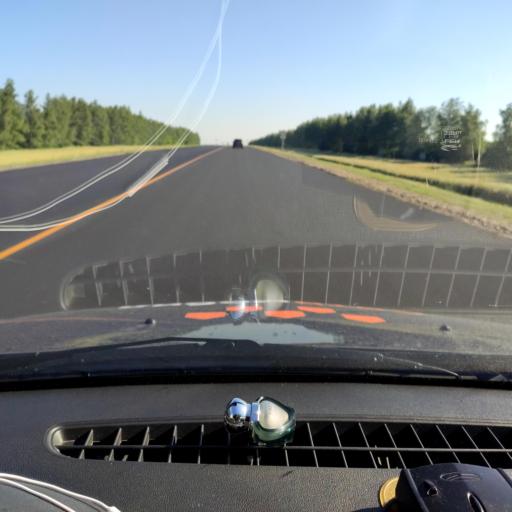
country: RU
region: Orjol
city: Zmiyevka
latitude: 52.7628
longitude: 36.3213
